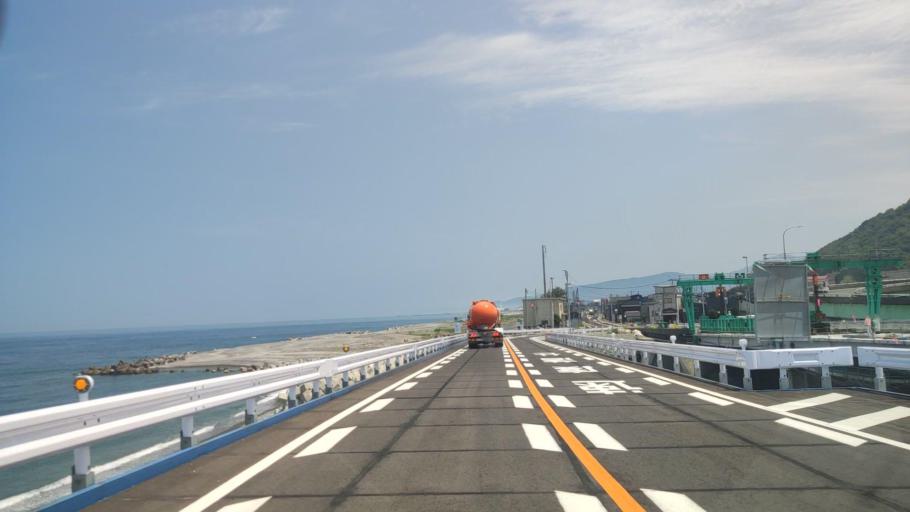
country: JP
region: Niigata
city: Itoigawa
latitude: 37.0233
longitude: 137.7899
